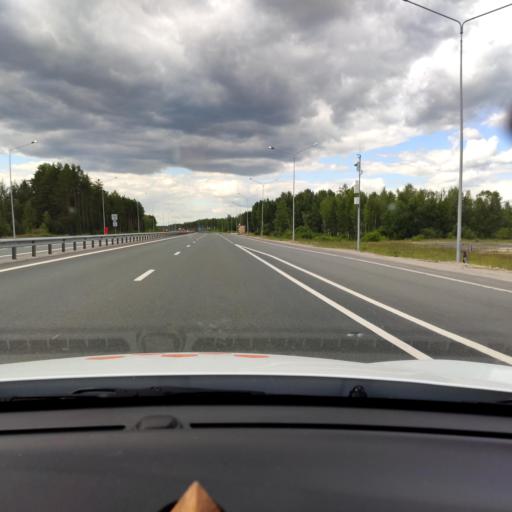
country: RU
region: Mariy-El
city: Surok
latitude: 56.4416
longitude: 48.1114
